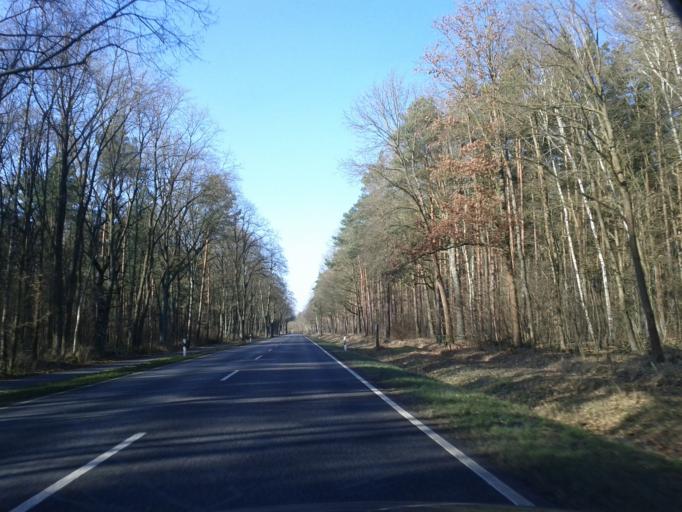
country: DE
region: Brandenburg
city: Spreenhagen
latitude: 52.4023
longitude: 13.8990
